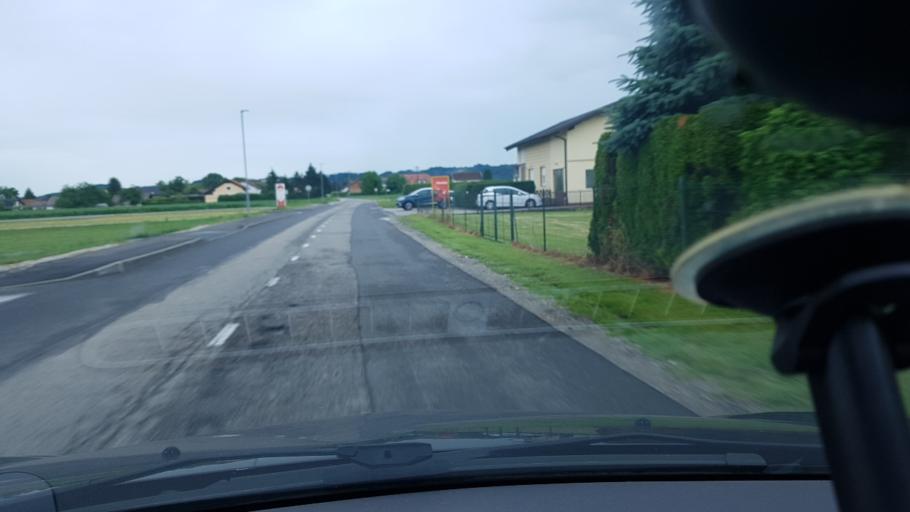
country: SI
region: Ptuj
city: Ptuj
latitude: 46.3870
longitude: 15.8732
